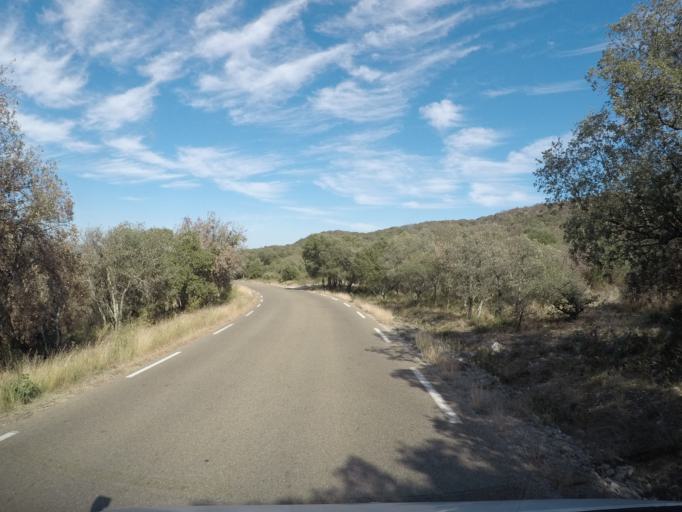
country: FR
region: Languedoc-Roussillon
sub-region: Departement du Gard
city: Boisset-et-Gaujac
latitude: 44.0114
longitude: 3.9920
